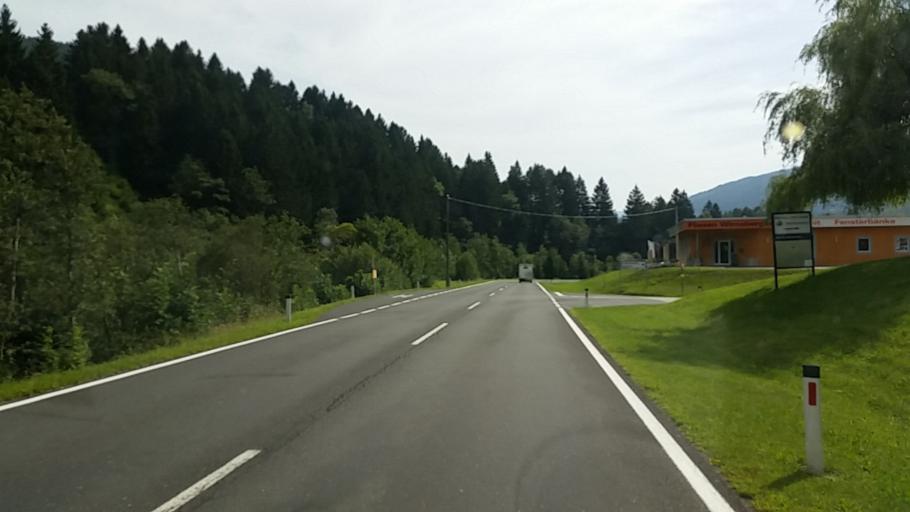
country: AT
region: Carinthia
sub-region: Politischer Bezirk Spittal an der Drau
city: Trebesing
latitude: 46.8922
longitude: 13.5243
